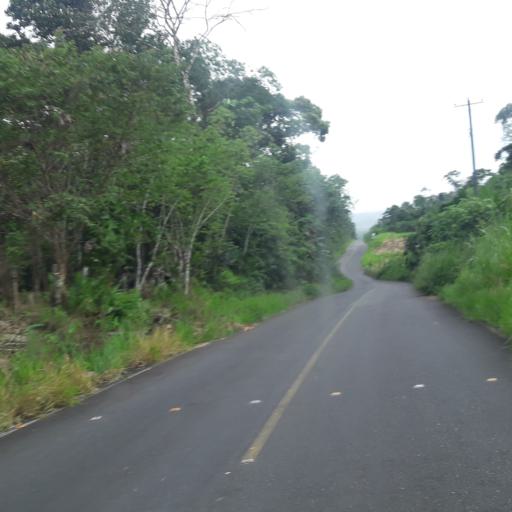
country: EC
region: Napo
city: Tena
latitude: -1.0524
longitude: -77.6636
